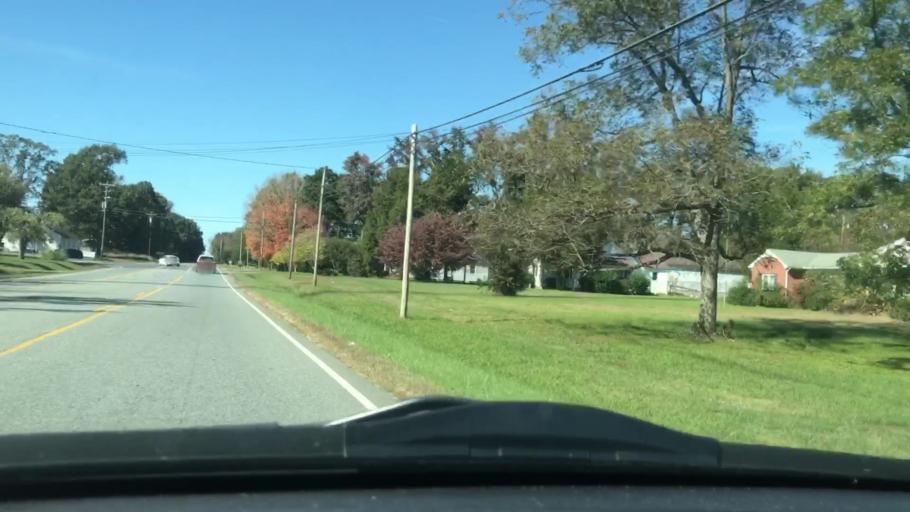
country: US
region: North Carolina
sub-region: Randolph County
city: Randleman
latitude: 35.8145
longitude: -79.8403
